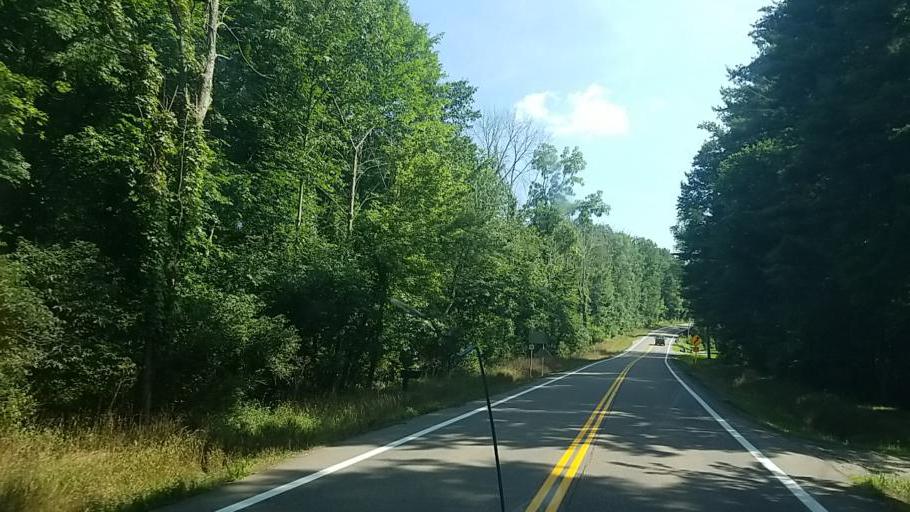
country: US
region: Ohio
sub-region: Knox County
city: Oak Hill
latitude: 40.3929
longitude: -82.2782
